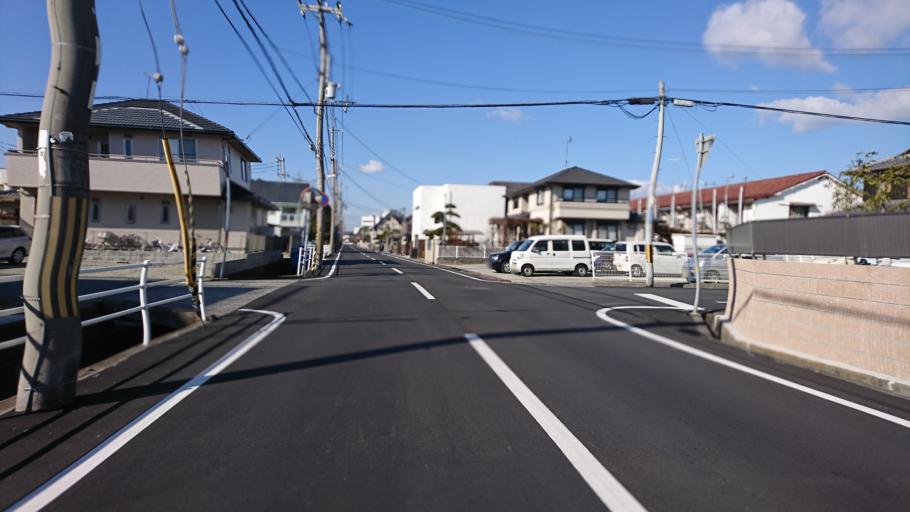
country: JP
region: Hyogo
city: Kakogawacho-honmachi
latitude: 34.7632
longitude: 134.7951
